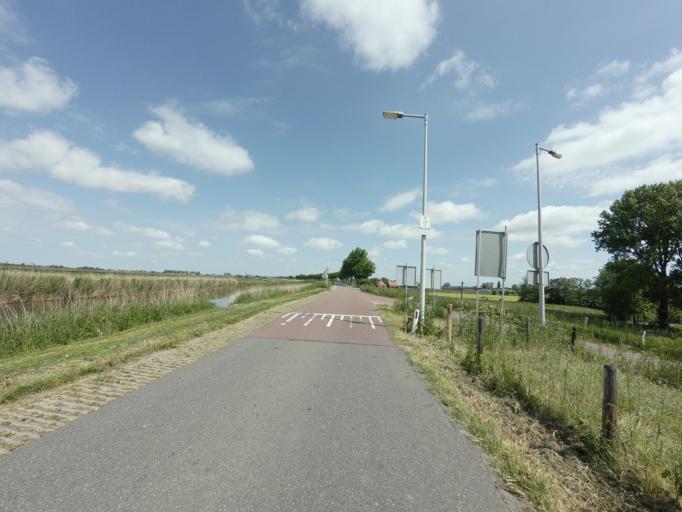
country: NL
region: North Holland
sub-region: Gemeente Beemster
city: Halfweg
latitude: 52.5844
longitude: 4.8851
